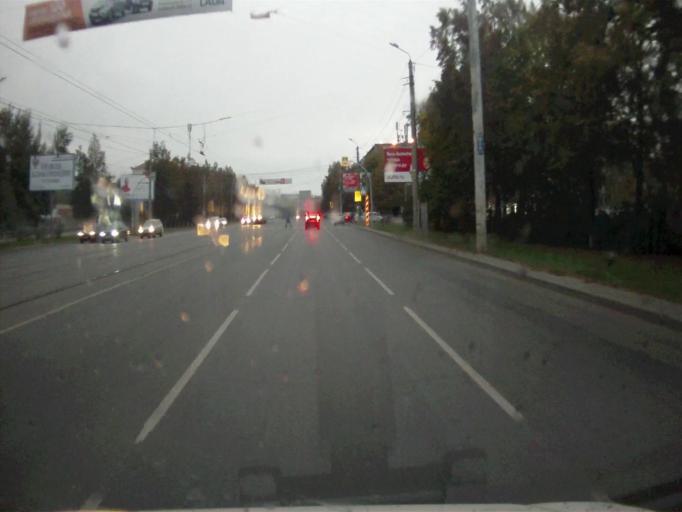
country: RU
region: Chelyabinsk
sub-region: Gorod Chelyabinsk
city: Chelyabinsk
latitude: 55.1760
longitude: 61.3998
